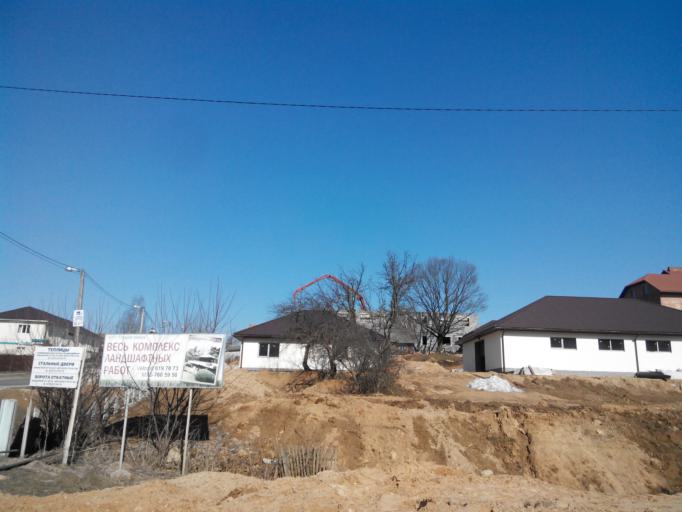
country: BY
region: Minsk
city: Zhdanovichy
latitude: 53.9152
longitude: 27.3909
